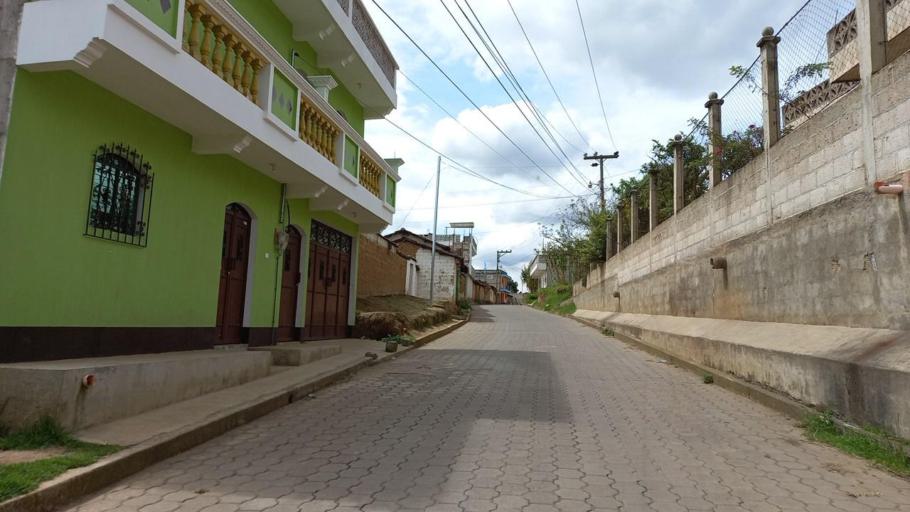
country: GT
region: Totonicapan
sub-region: Municipio de San Andres Xecul
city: San Andres Xecul
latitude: 14.8905
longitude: -91.4752
